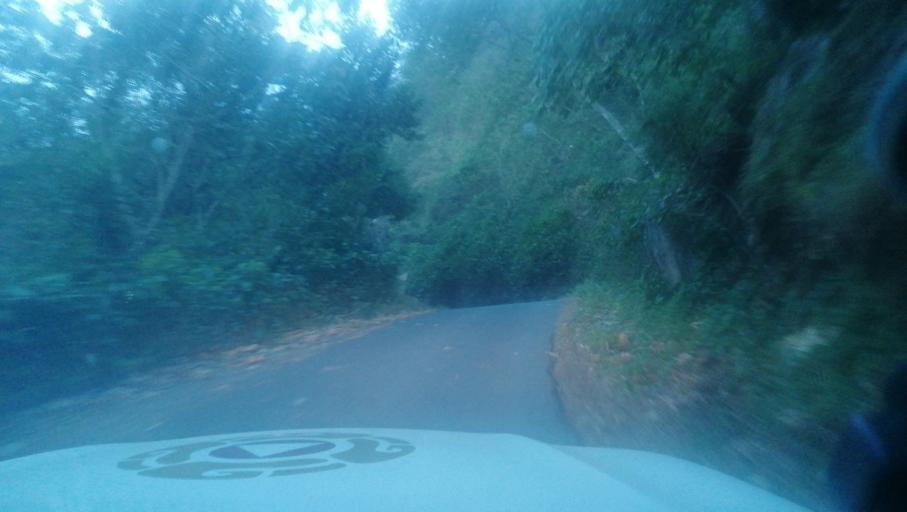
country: MX
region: Chiapas
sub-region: Cacahoatan
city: Benito Juarez
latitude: 15.1239
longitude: -92.2091
